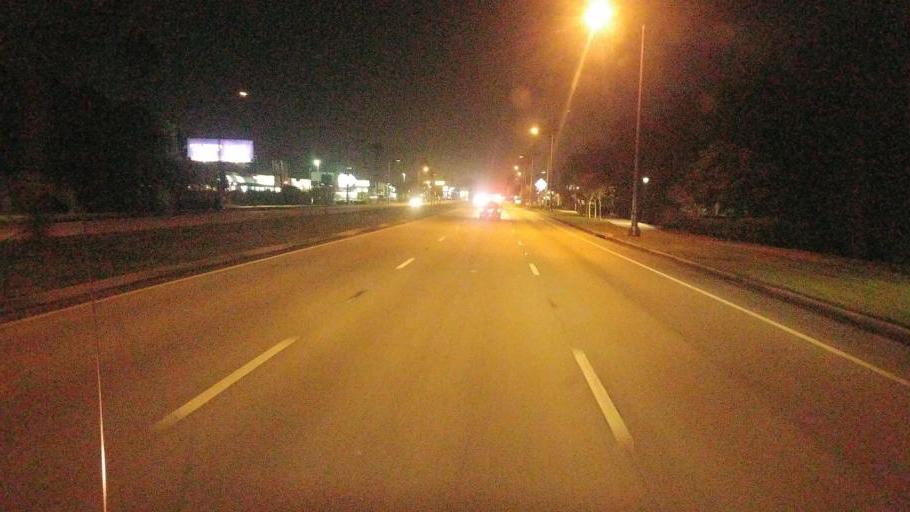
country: US
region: Florida
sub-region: Osceola County
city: Celebration
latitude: 28.3328
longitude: -81.5059
